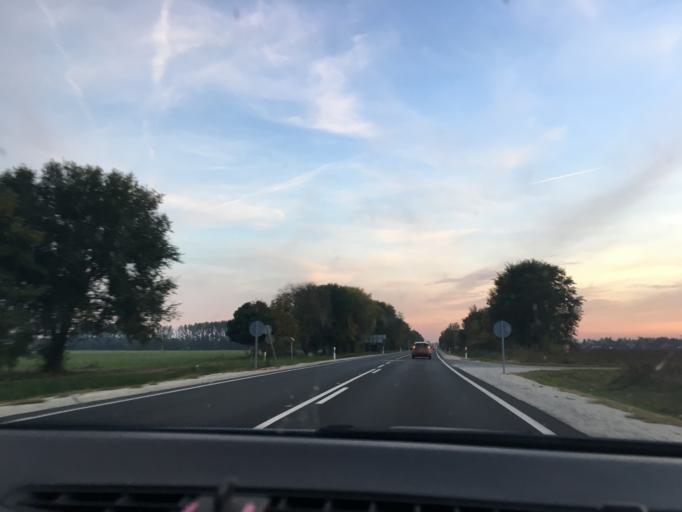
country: HU
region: Hajdu-Bihar
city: Hajduhadhaz
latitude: 47.6556
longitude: 21.6615
